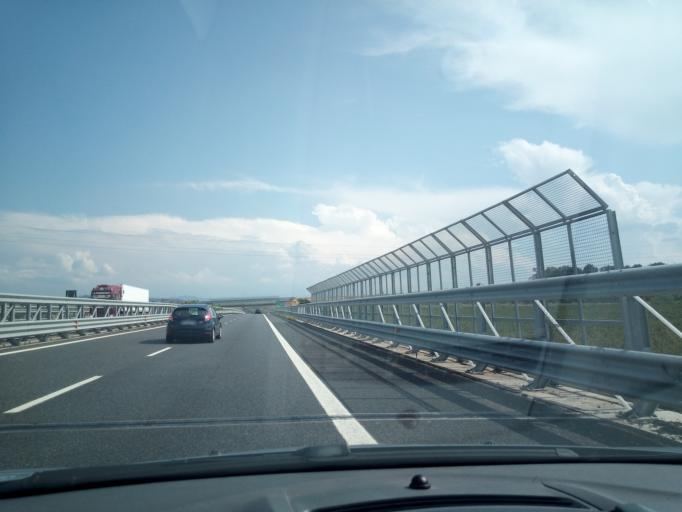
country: IT
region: Calabria
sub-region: Provincia di Cosenza
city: Firmo
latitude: 39.7192
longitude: 16.2402
